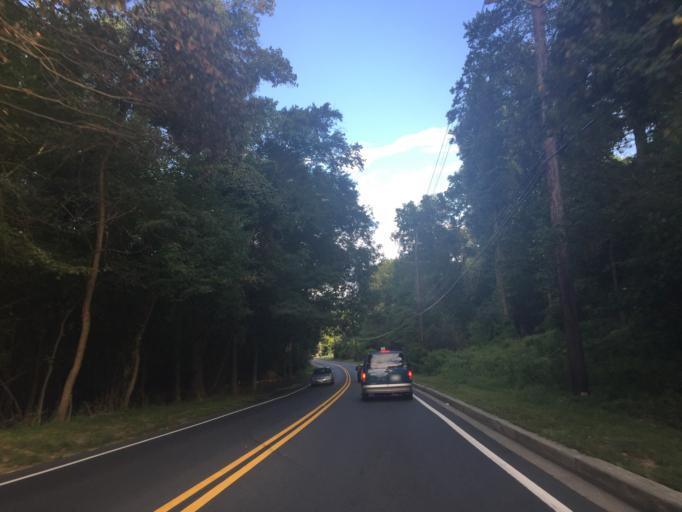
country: US
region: Maryland
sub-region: Montgomery County
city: Redland
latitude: 39.1391
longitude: -77.1318
